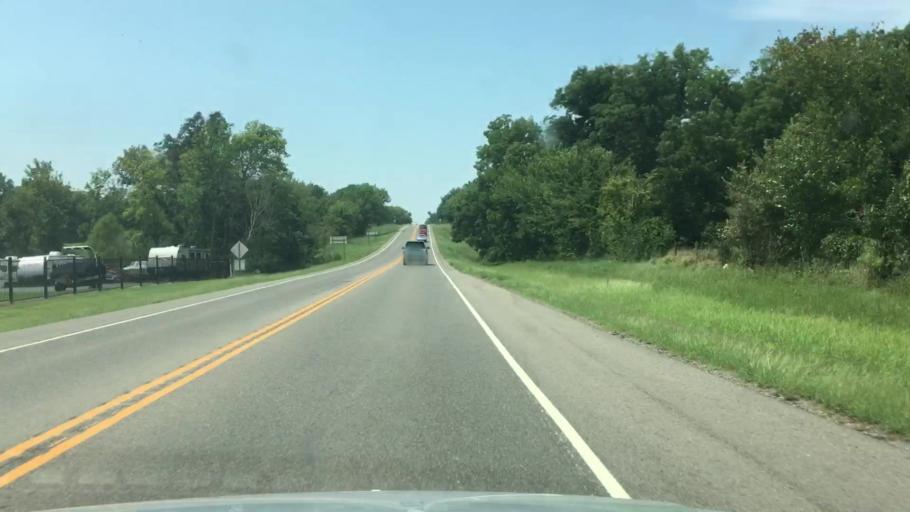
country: US
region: Oklahoma
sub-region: Wagoner County
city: Wagoner
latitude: 35.9406
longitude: -95.2986
